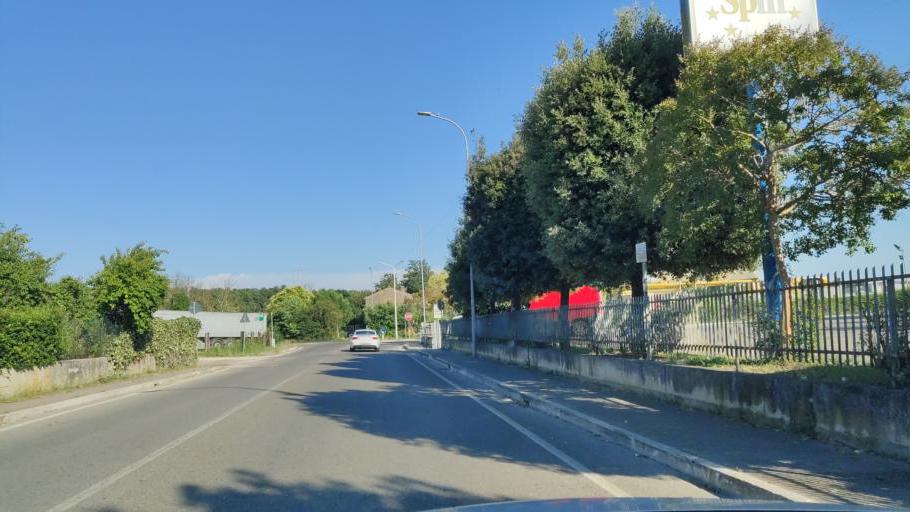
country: IT
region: Latium
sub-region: Provincia di Viterbo
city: Orte
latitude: 42.4660
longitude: 12.3935
